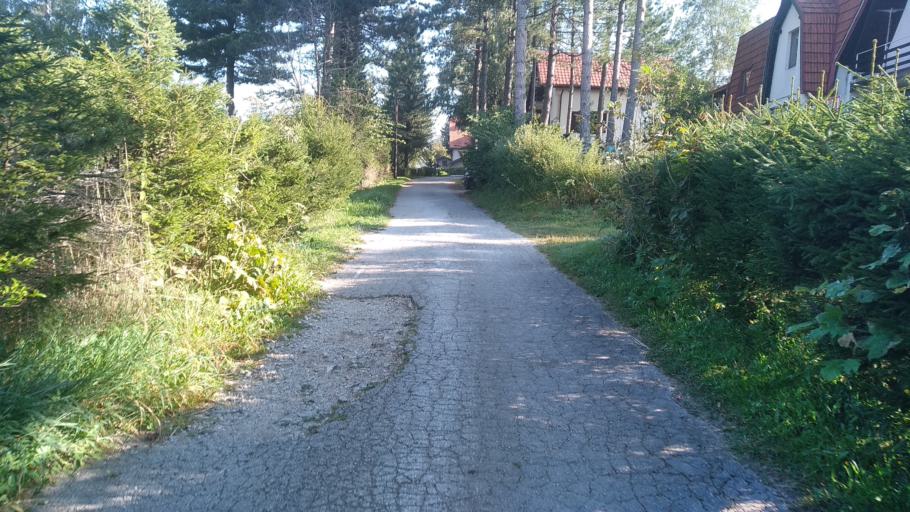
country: RS
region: Central Serbia
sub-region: Zlatiborski Okrug
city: Cajetina
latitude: 43.7348
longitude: 19.7152
